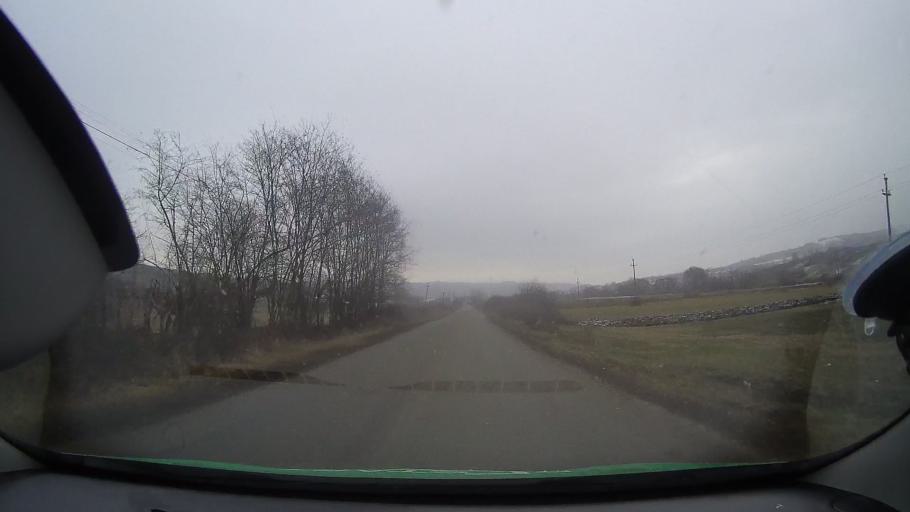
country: RO
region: Alba
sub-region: Comuna Farau
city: Farau
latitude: 46.3388
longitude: 23.9872
